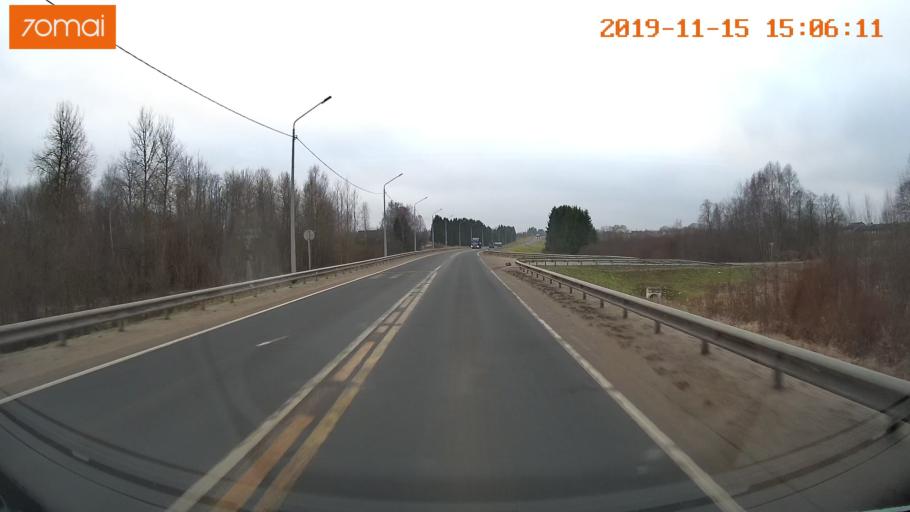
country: RU
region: Jaroslavl
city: Prechistoye
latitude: 58.3953
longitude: 40.3139
